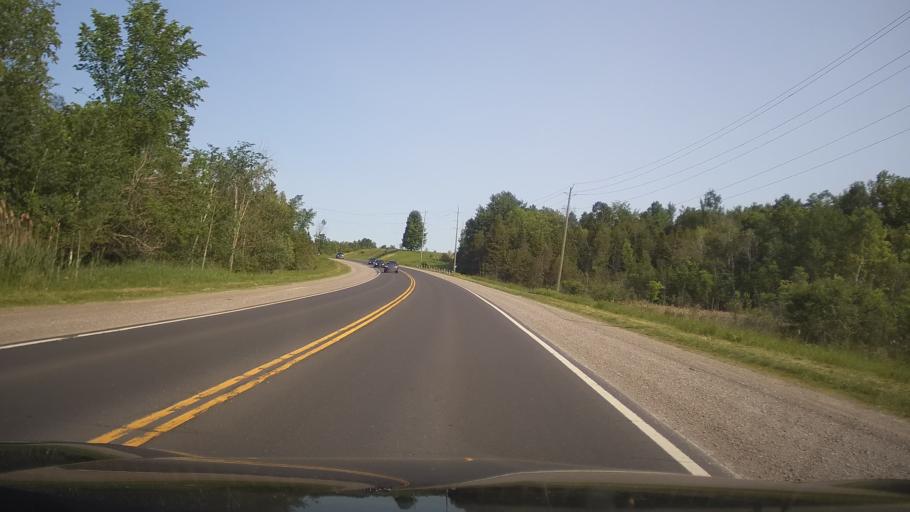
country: CA
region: Ontario
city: Peterborough
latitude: 44.2725
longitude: -78.4106
